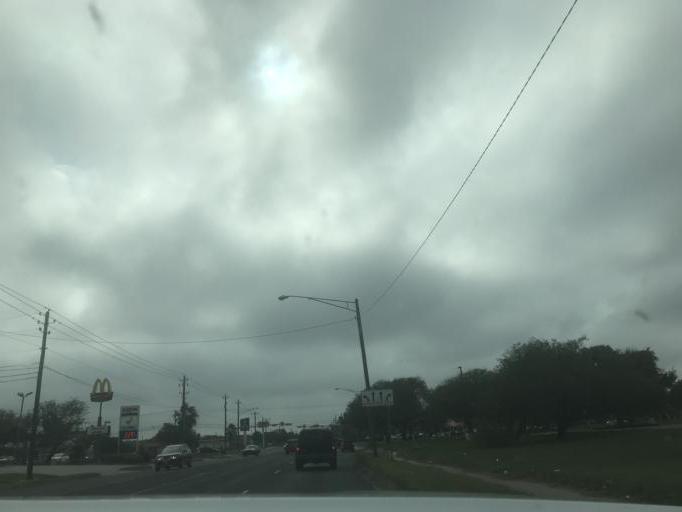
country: US
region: Texas
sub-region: Nueces County
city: Corpus Christi
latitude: 27.6798
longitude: -97.3689
